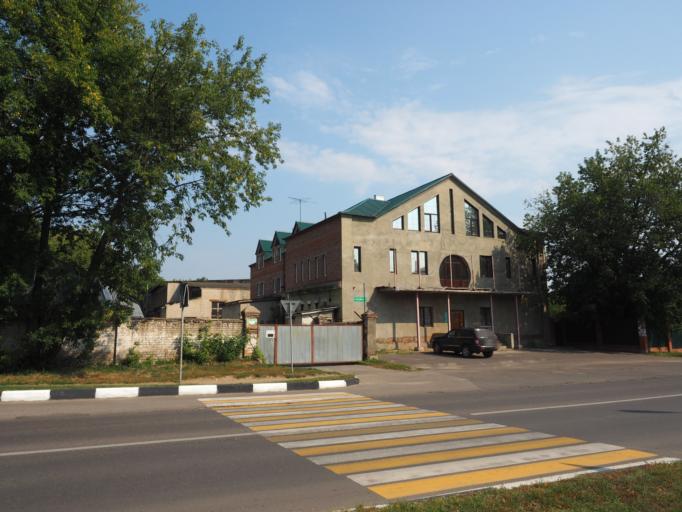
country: RU
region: Moskovskaya
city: Udel'naya
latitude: 55.6367
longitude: 38.0100
